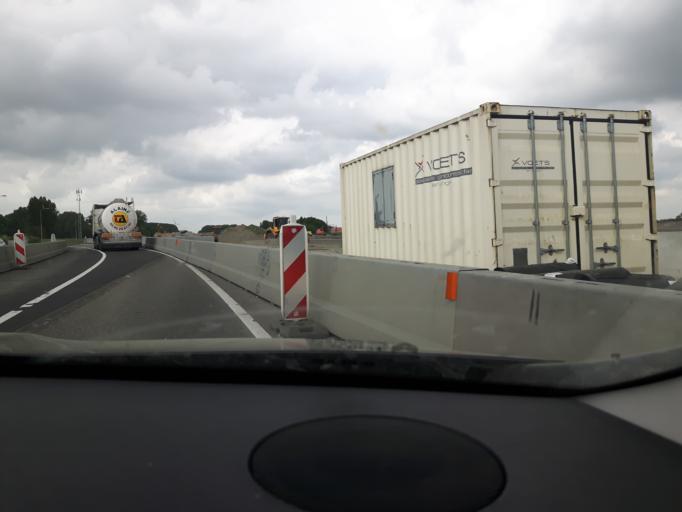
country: NL
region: Zeeland
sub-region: Gemeente Borsele
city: Borssele
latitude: 51.4584
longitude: 3.7396
